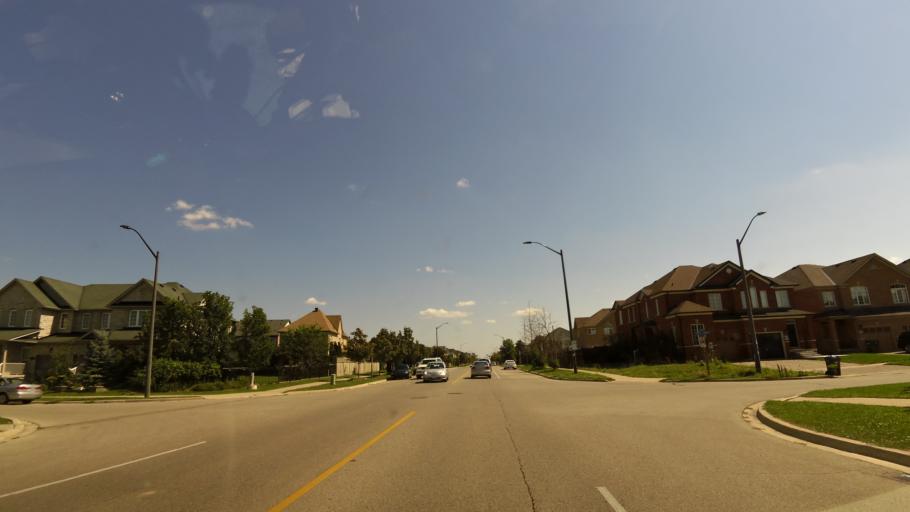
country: CA
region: Ontario
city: Mississauga
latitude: 43.5635
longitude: -79.7481
